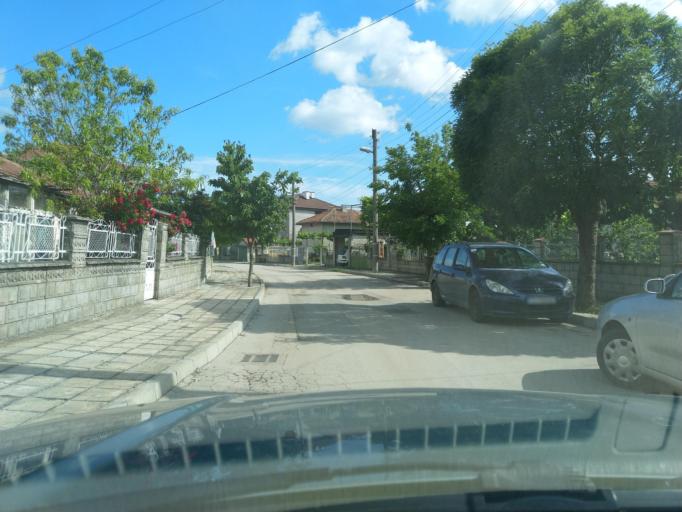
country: BG
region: Dobrich
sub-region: Obshtina Kavarna
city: Kavarna
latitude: 43.4336
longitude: 28.3315
